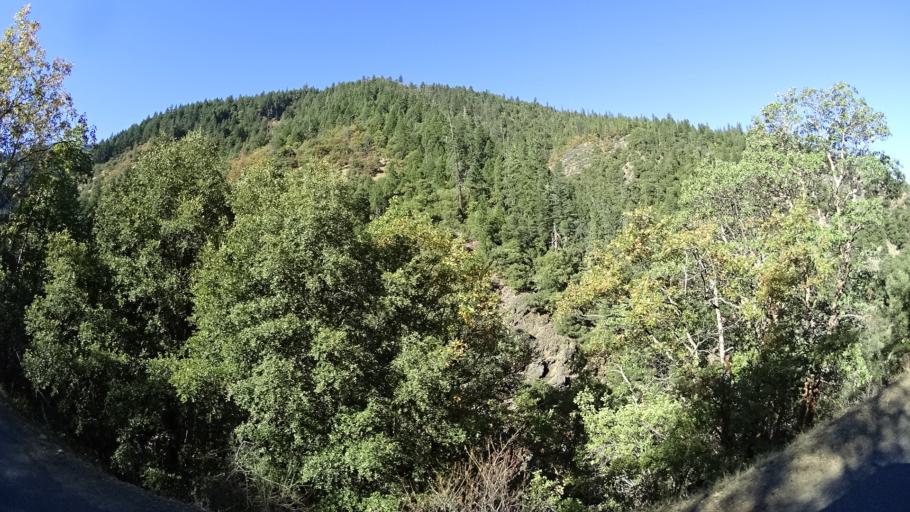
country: US
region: California
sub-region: Humboldt County
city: Willow Creek
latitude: 41.1834
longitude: -123.2175
